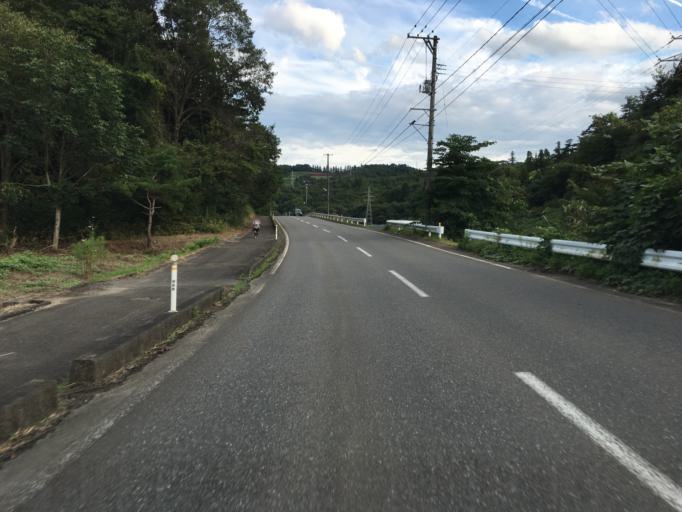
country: JP
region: Fukushima
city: Hobaramachi
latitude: 37.7872
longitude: 140.5437
